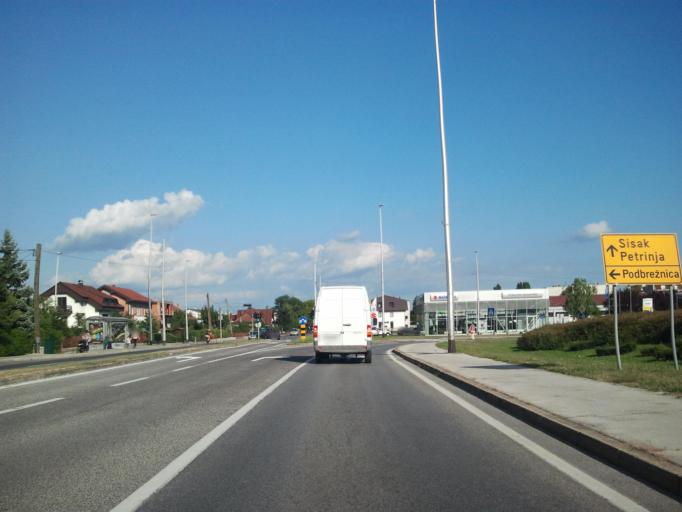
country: HR
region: Zagrebacka
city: Gradici
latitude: 45.7211
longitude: 16.0538
